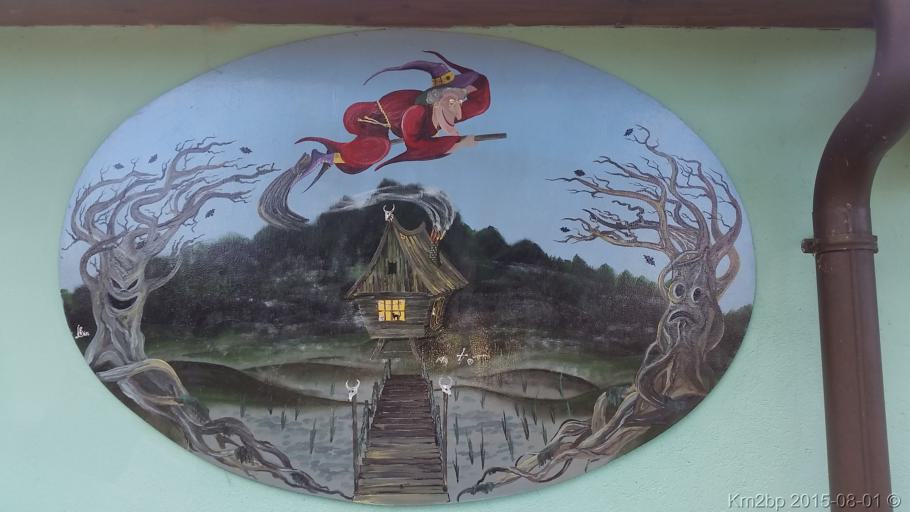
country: DE
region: Brandenburg
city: Vogelsang
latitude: 52.2411
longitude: 14.7023
